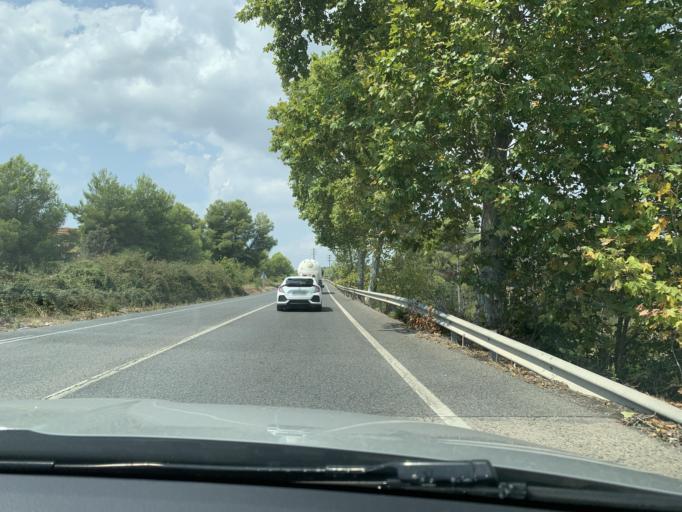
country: ES
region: Catalonia
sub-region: Provincia de Tarragona
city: Altafulla
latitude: 41.1392
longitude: 1.3517
